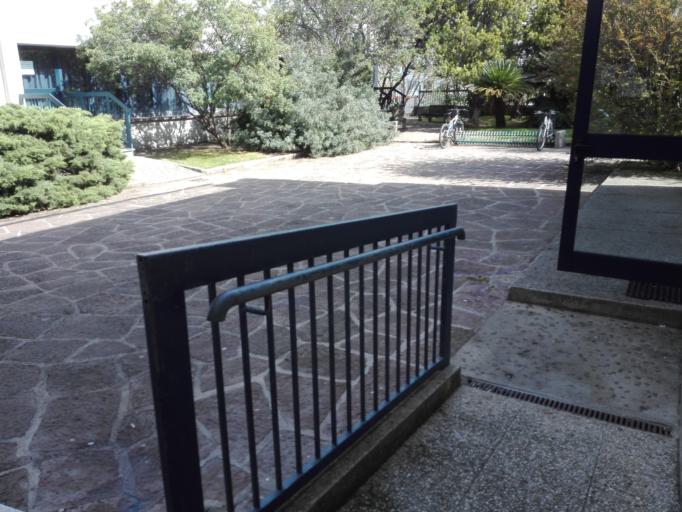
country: IT
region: Sardinia
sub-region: Provincia di Sassari
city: Sassari
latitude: 40.7174
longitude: 8.5536
